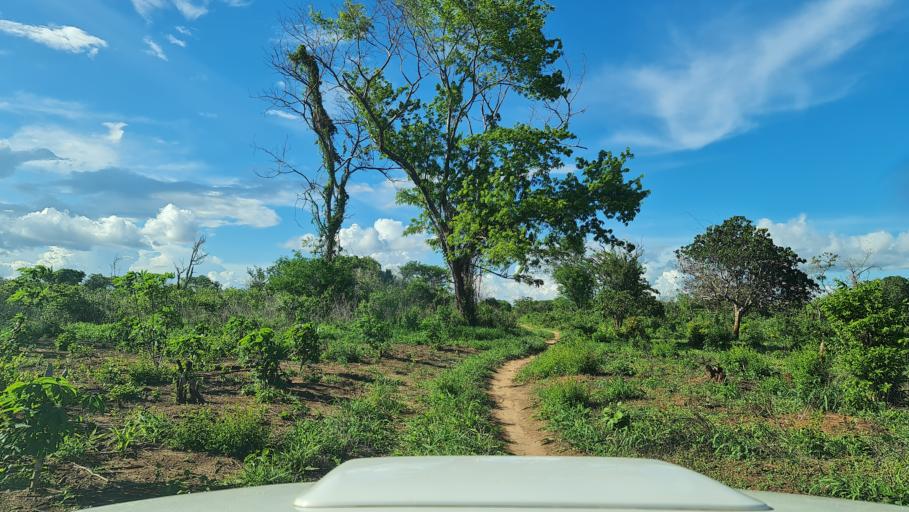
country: MZ
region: Nampula
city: Ilha de Mocambique
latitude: -15.2666
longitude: 40.1863
